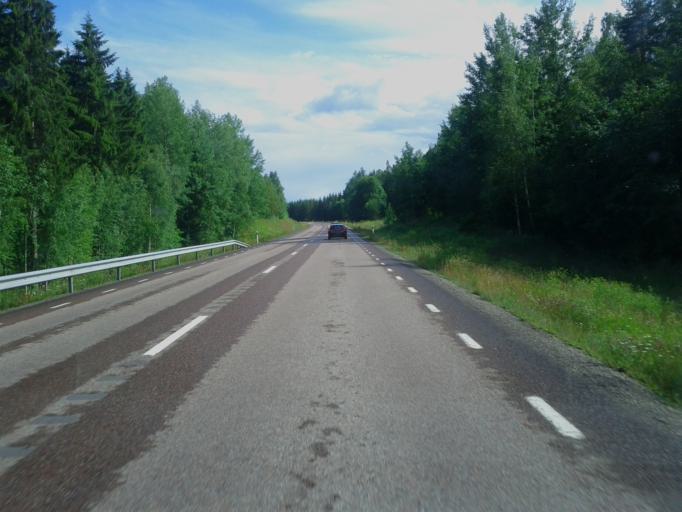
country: SE
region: Dalarna
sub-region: Faluns Kommun
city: Falun
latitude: 60.6563
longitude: 15.5543
